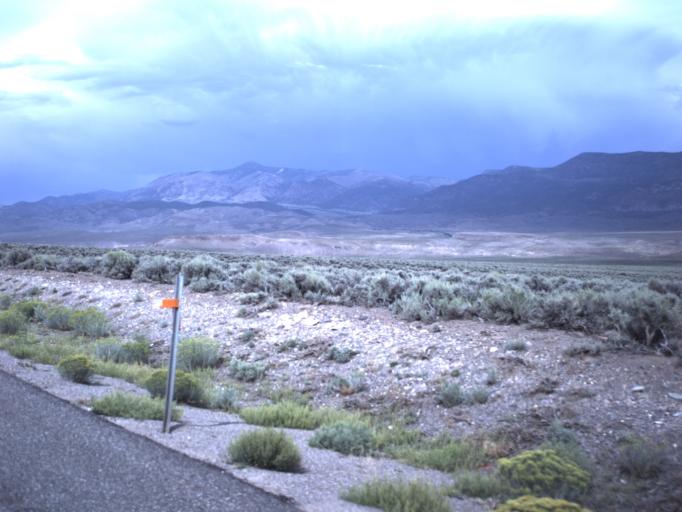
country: US
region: Utah
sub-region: Piute County
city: Junction
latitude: 38.3363
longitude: -112.2176
